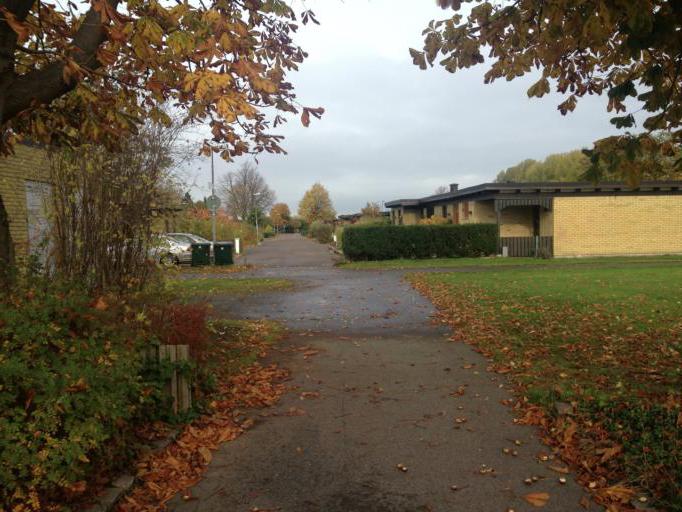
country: SE
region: Skane
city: Bjarred
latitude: 55.7253
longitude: 13.0244
